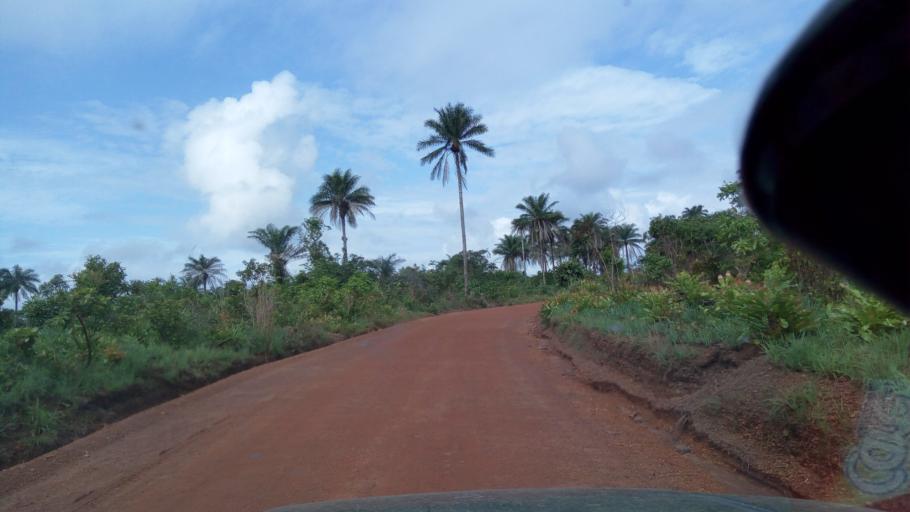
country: SL
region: Northern Province
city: Pepel
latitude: 8.6501
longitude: -13.0105
